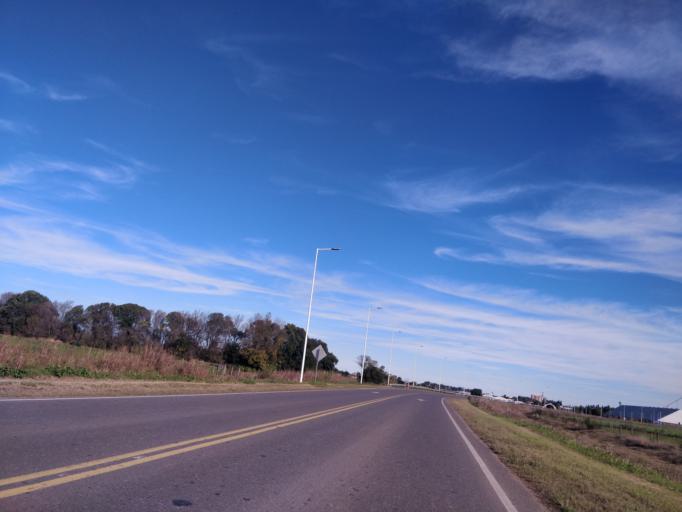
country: AR
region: Cordoba
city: Leones
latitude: -32.6452
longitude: -62.2911
